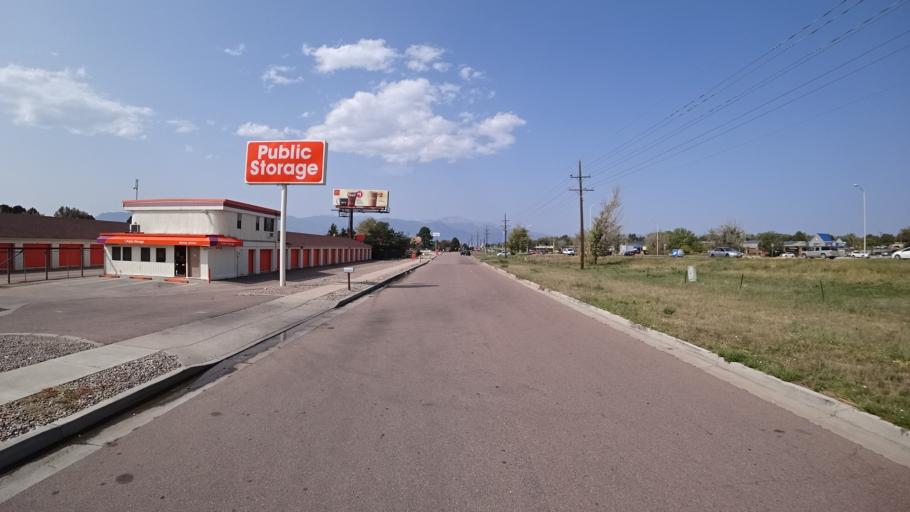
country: US
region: Colorado
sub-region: El Paso County
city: Cimarron Hills
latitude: 38.8394
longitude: -104.7450
